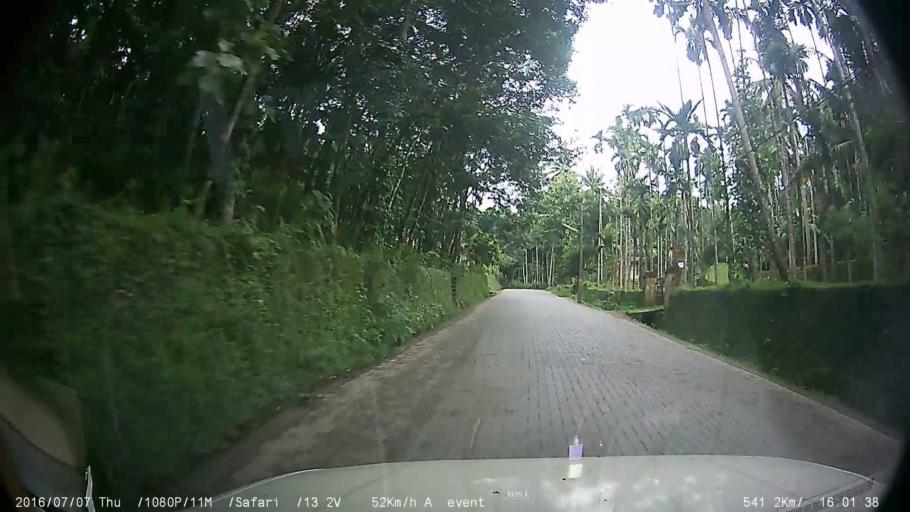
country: IN
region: Kerala
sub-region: Ernakulam
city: Piravam
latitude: 9.8499
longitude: 76.6042
